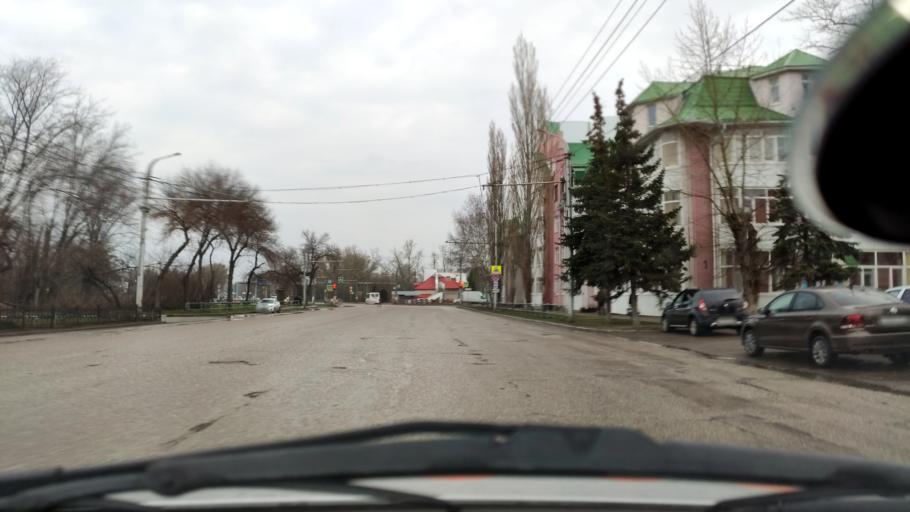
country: RU
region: Bashkortostan
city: Sterlitamak
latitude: 53.6532
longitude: 55.9478
